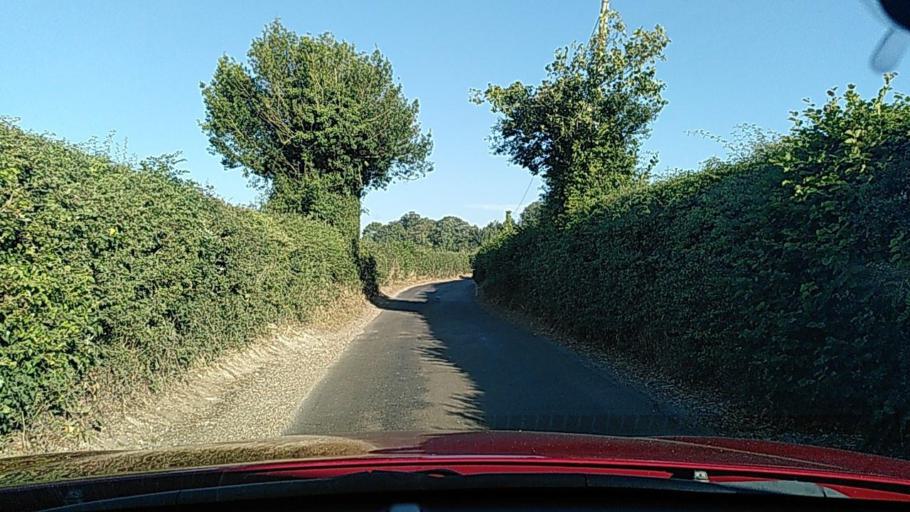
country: GB
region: England
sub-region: Wokingham
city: Sonning
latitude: 51.4907
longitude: -0.9427
